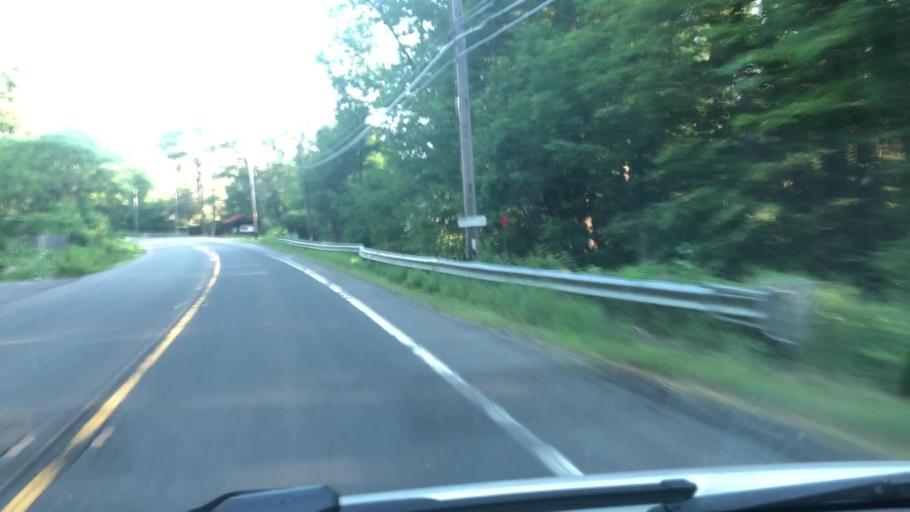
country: US
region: Massachusetts
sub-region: Hampshire County
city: Williamsburg
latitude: 42.4126
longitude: -72.7591
